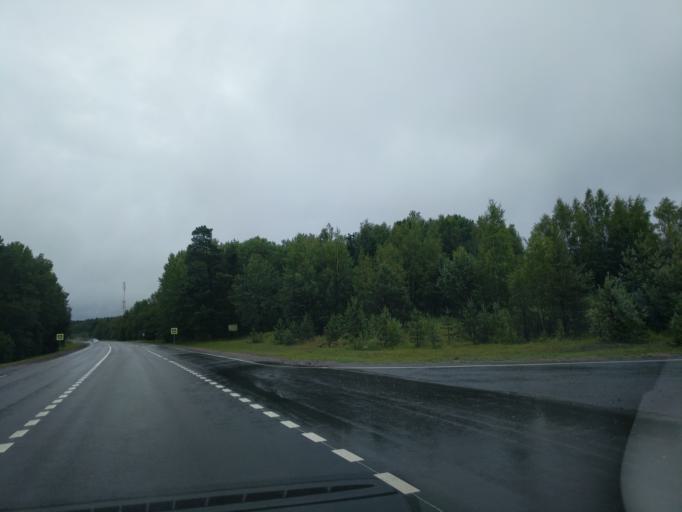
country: BY
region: Minsk
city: Syomkava
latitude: 54.1605
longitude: 27.5021
